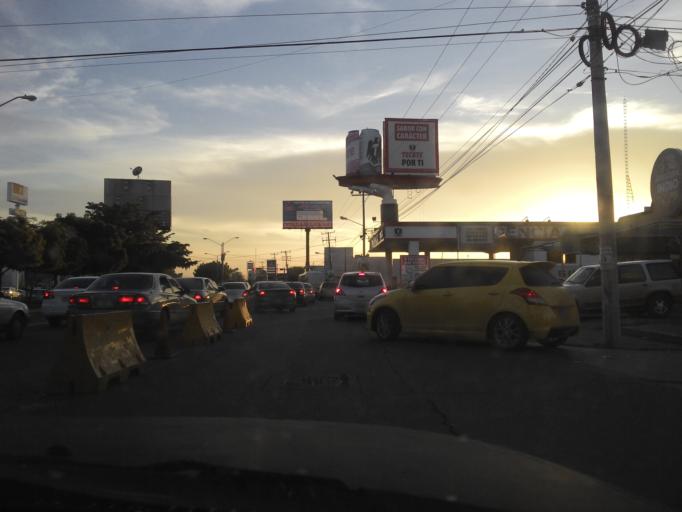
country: MX
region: Sinaloa
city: Culiacan
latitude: 24.7972
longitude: -107.4006
